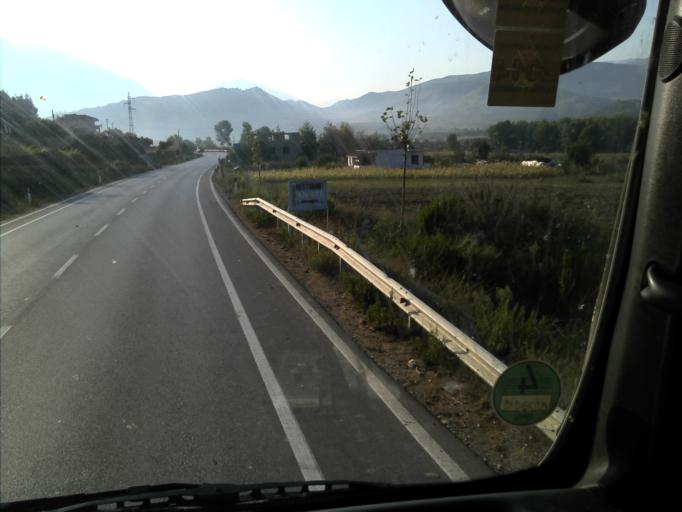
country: AL
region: Gjirokaster
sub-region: Rrethi i Tepelenes
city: Memaliaj
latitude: 40.3548
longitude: 19.9485
